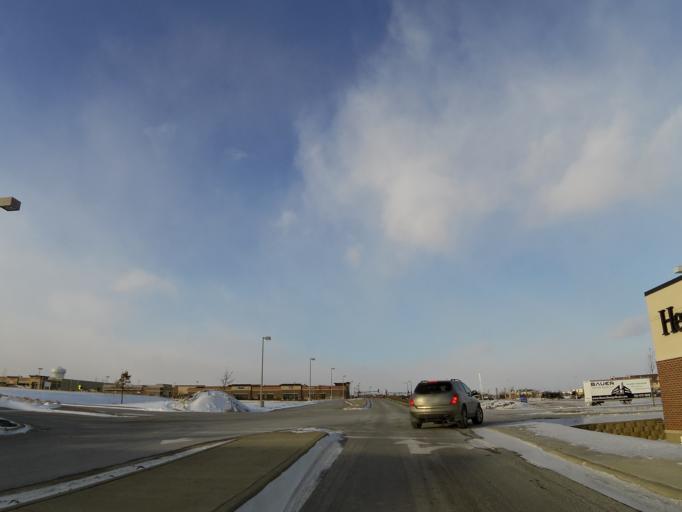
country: US
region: Minnesota
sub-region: Washington County
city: Woodbury
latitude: 44.9387
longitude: -92.9055
